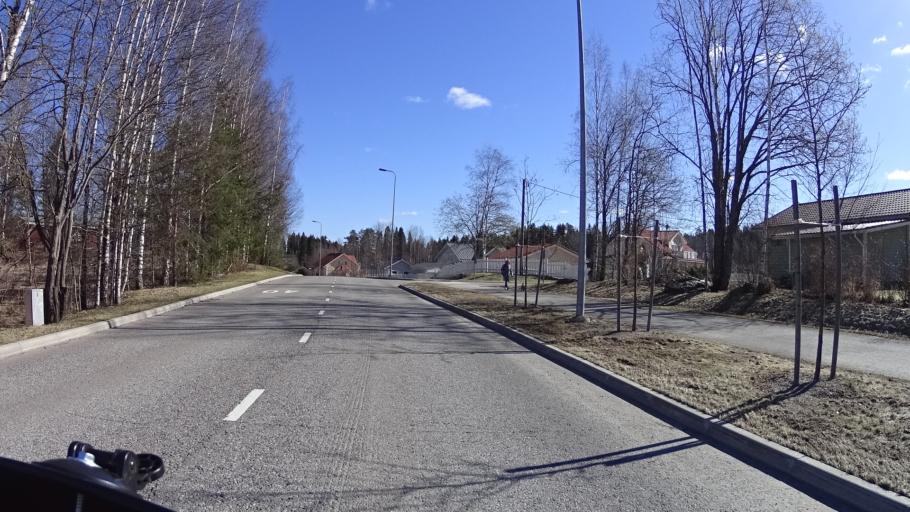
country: FI
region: Uusimaa
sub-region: Helsinki
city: Kauniainen
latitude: 60.3251
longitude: 24.7151
